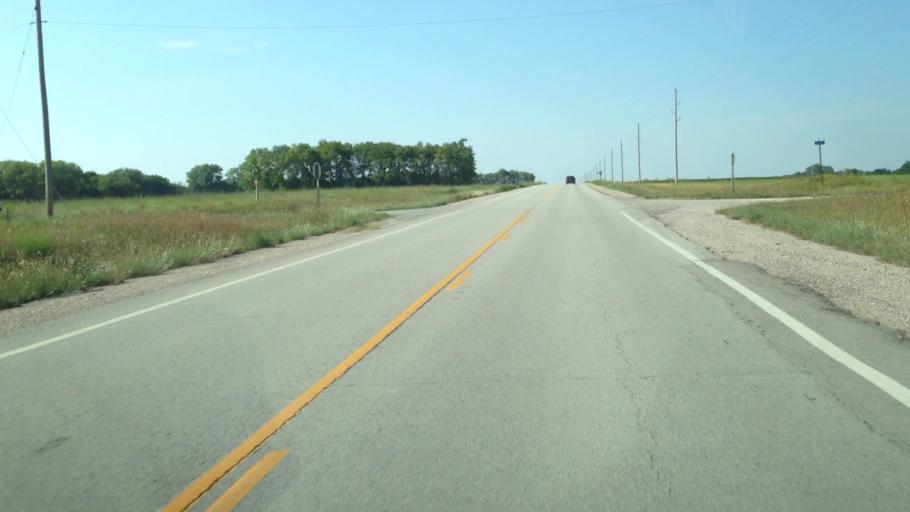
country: US
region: Kansas
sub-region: Anderson County
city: Garnett
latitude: 38.0410
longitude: -95.1697
